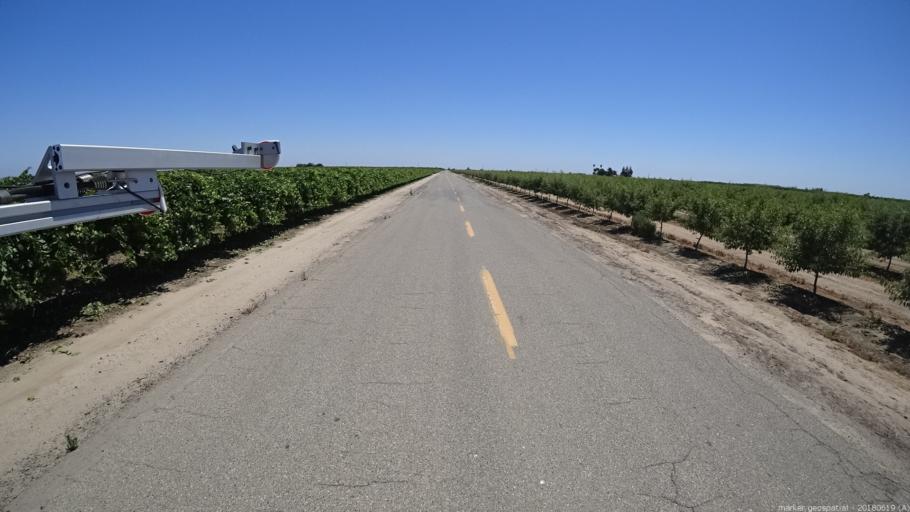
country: US
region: California
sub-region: Madera County
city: Parkwood
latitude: 36.8731
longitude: -120.0624
